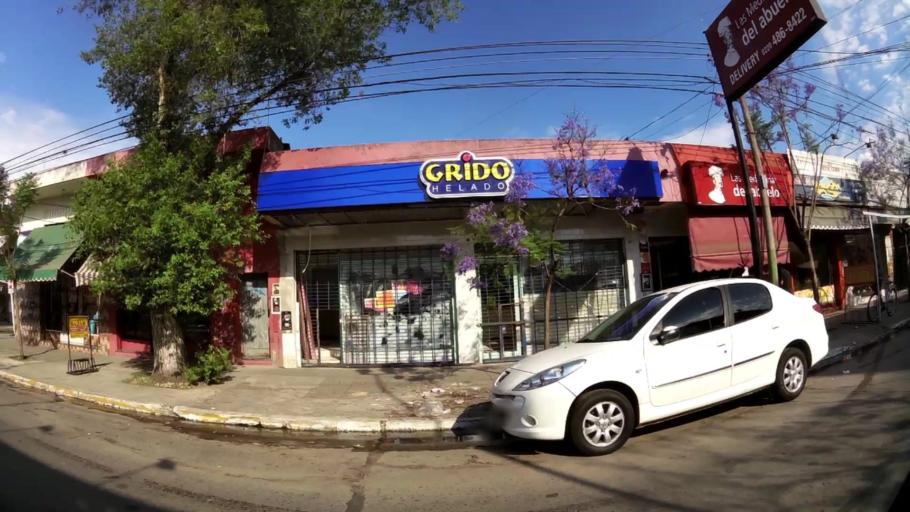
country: AR
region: Buenos Aires
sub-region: Partido de Merlo
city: Merlo
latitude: -34.6602
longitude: -58.7259
